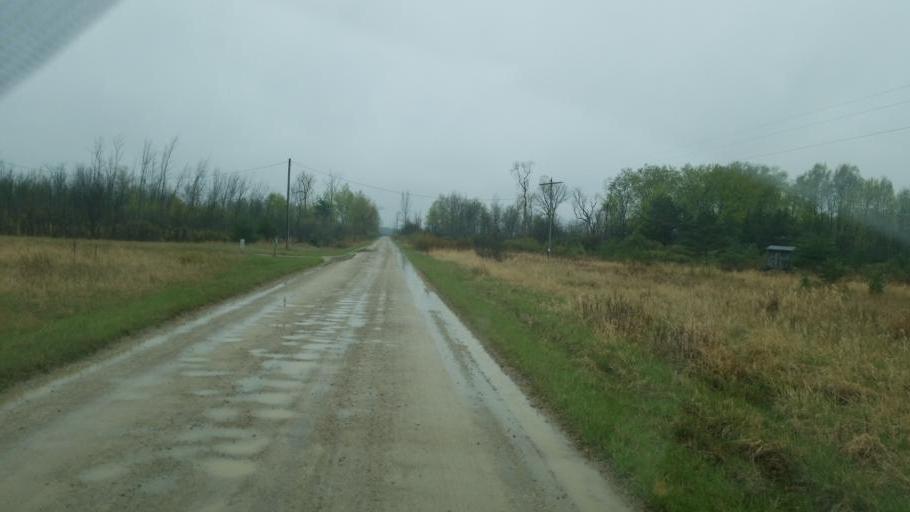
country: US
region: Michigan
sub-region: Montcalm County
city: Lakeview
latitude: 43.4950
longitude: -85.3186
